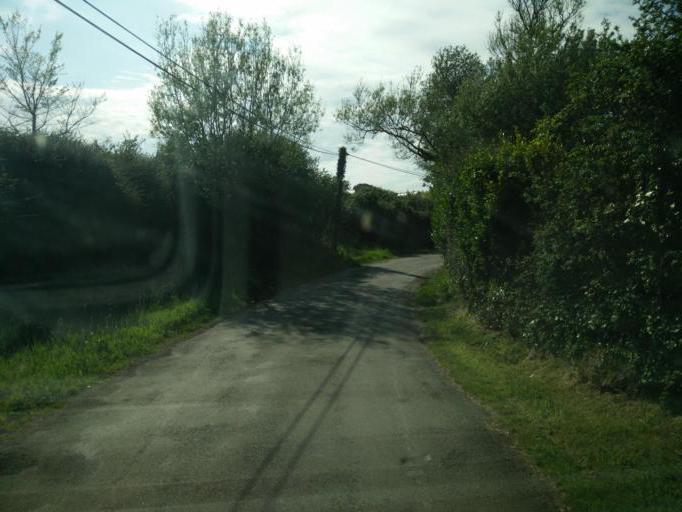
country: FR
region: Brittany
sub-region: Departement du Finistere
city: Crozon
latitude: 48.2343
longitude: -4.5464
